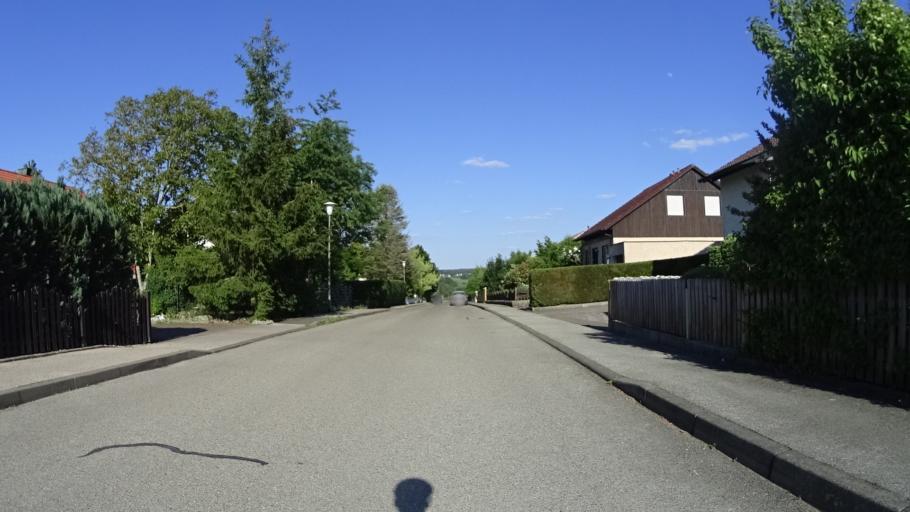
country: DE
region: Bavaria
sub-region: Regierungsbezirk Mittelfranken
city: Feuchtwangen
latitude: 49.1631
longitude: 10.3453
